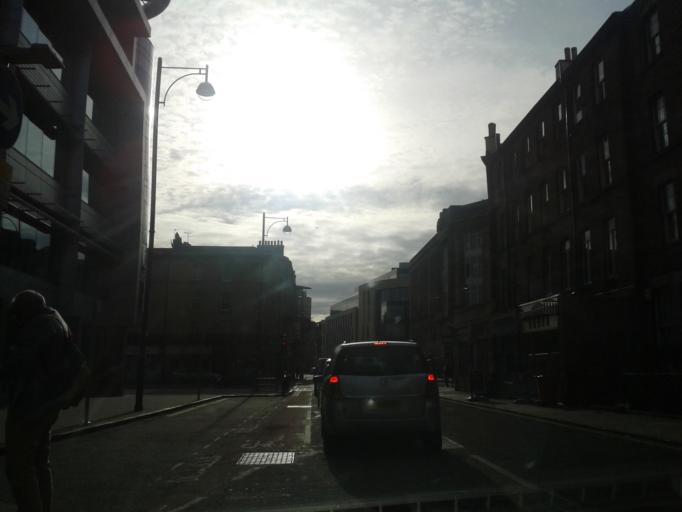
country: GB
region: Scotland
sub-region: Edinburgh
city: Edinburgh
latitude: 55.9451
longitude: -3.2042
